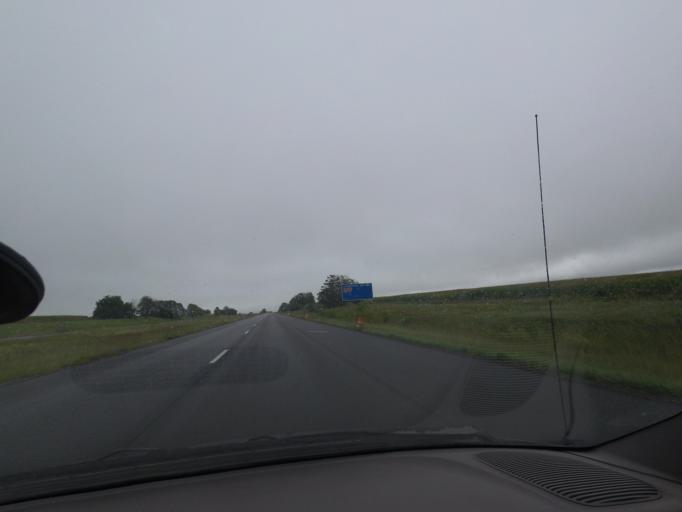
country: US
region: Illinois
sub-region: Macon County
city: Harristown
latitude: 39.8312
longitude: -89.0917
